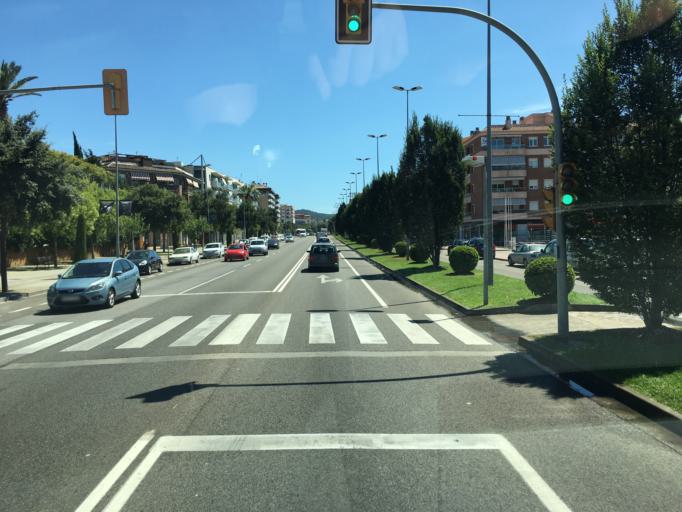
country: ES
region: Catalonia
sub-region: Provincia de Girona
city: Lloret de Mar
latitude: 41.6983
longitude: 2.8266
